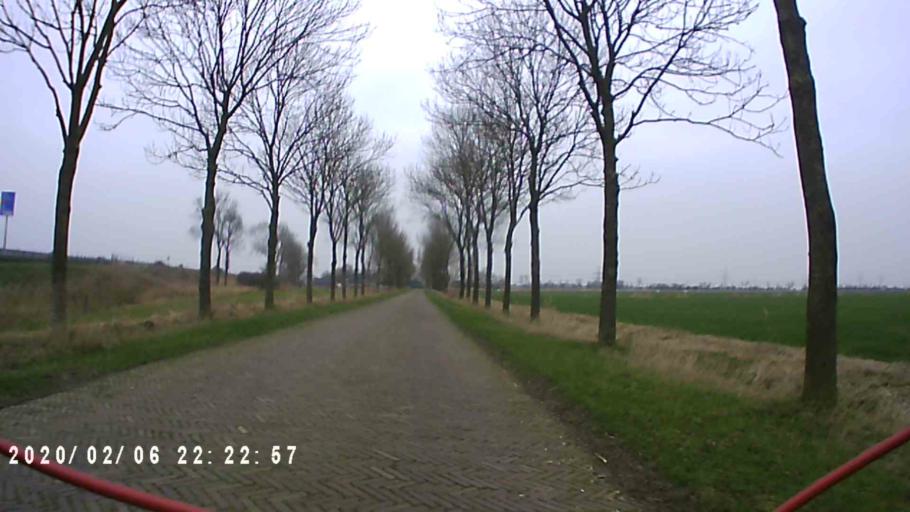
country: NL
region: Groningen
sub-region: Gemeente Zuidhorn
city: Aduard
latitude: 53.2450
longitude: 6.4857
